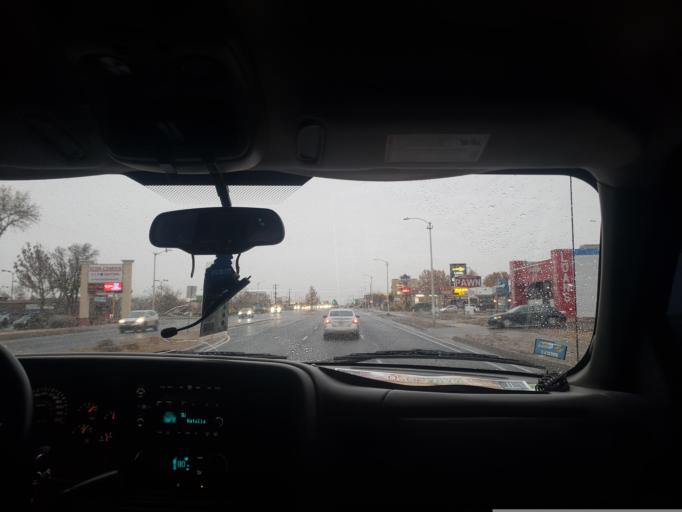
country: US
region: New Mexico
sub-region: Bernalillo County
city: North Valley
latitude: 35.1347
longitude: -106.5862
